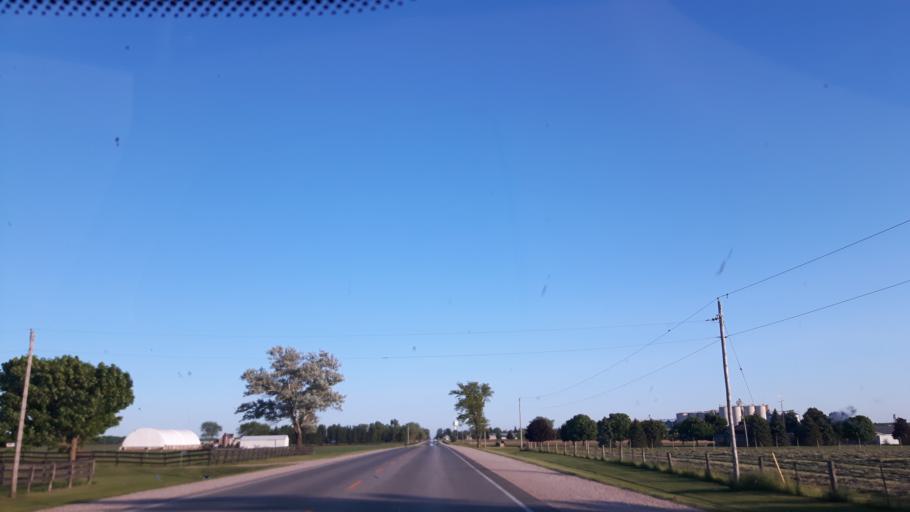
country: CA
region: Ontario
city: Bluewater
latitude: 43.4502
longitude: -81.5018
